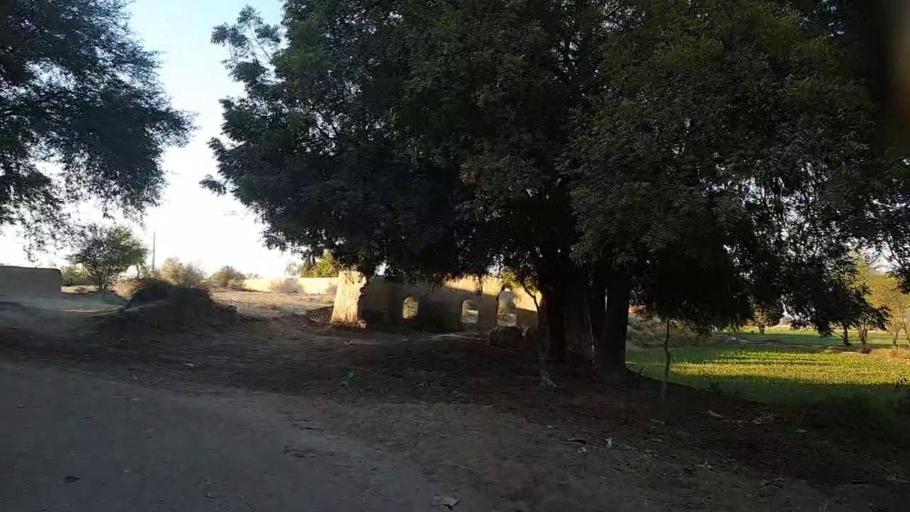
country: PK
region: Sindh
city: Khairpur
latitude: 27.9118
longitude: 69.6823
